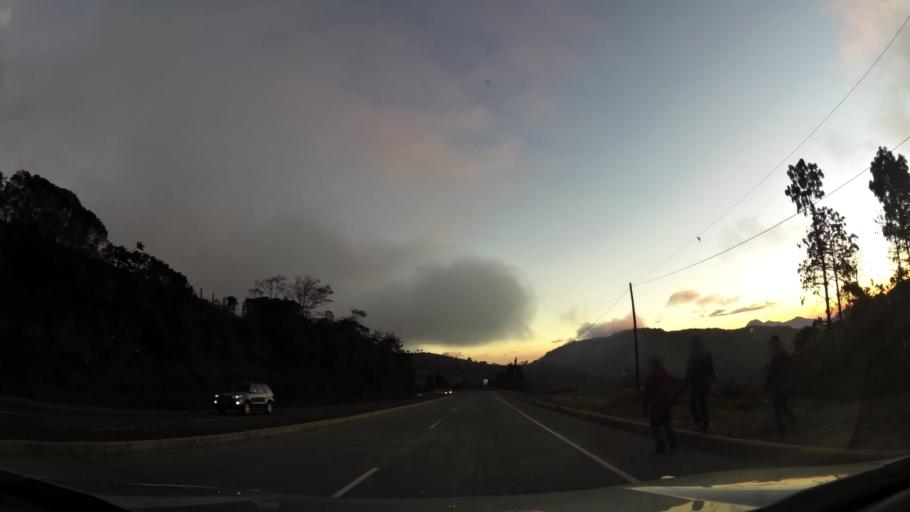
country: GT
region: Solola
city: Concepcion
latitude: 14.8325
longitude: -91.0947
